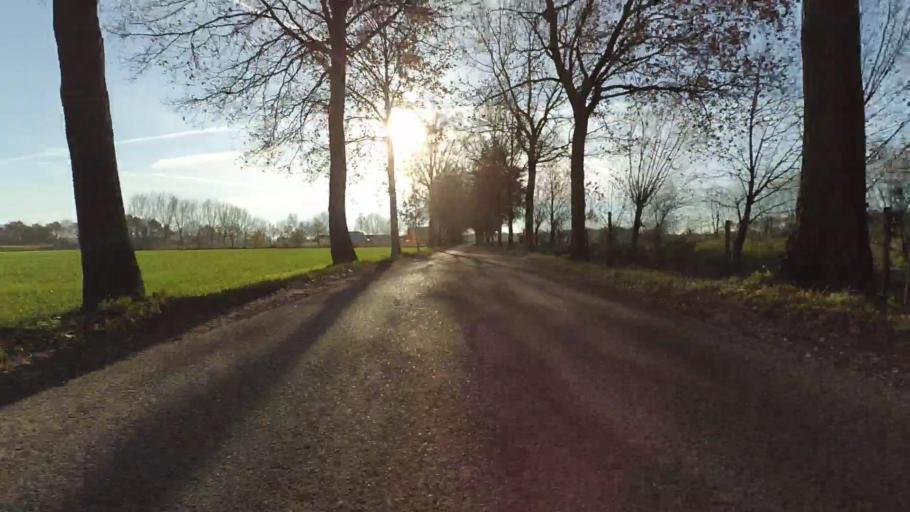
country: NL
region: Utrecht
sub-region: Gemeente Utrechtse Heuvelrug
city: Overberg
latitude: 52.0533
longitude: 5.4813
